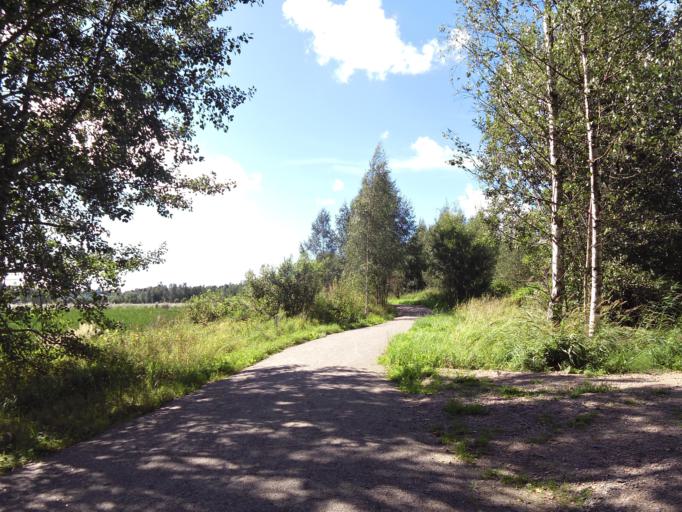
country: FI
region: Uusimaa
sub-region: Helsinki
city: Koukkuniemi
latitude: 60.1545
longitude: 24.7176
